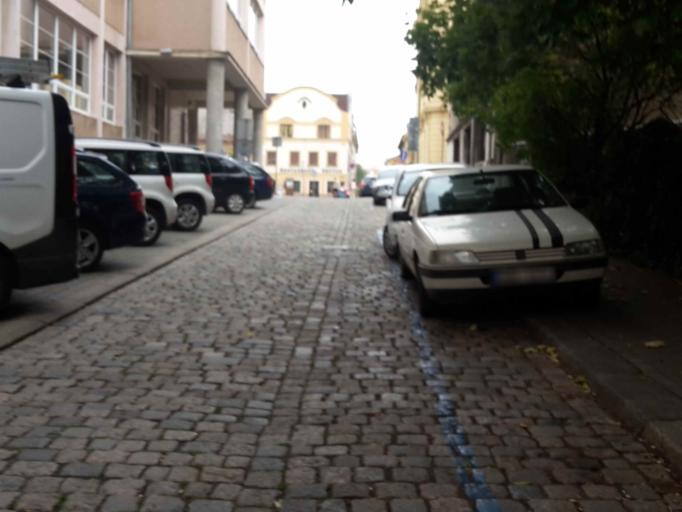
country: CZ
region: Liberecky
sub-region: Okres Liberec
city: Liberec
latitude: 50.7707
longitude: 15.0608
